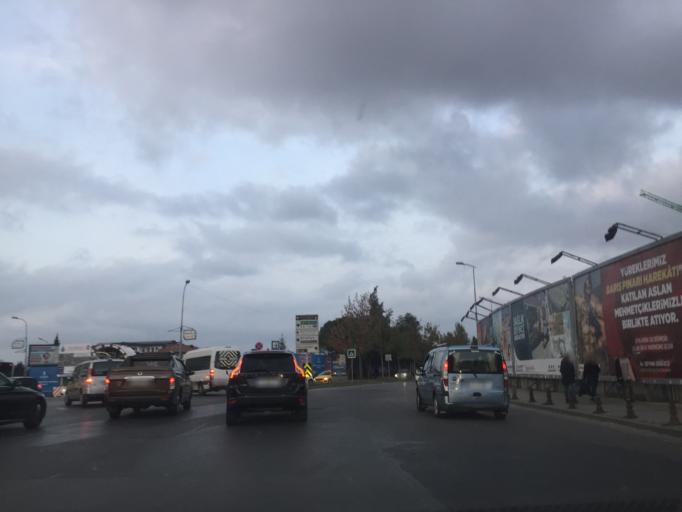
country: TR
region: Istanbul
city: Samandira
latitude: 40.9903
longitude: 29.2292
